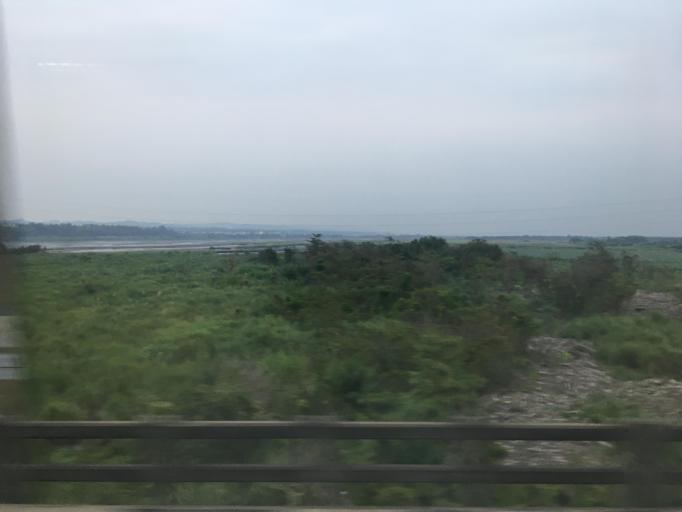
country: TW
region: Taiwan
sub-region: Pingtung
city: Pingtung
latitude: 22.6622
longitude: 120.4364
